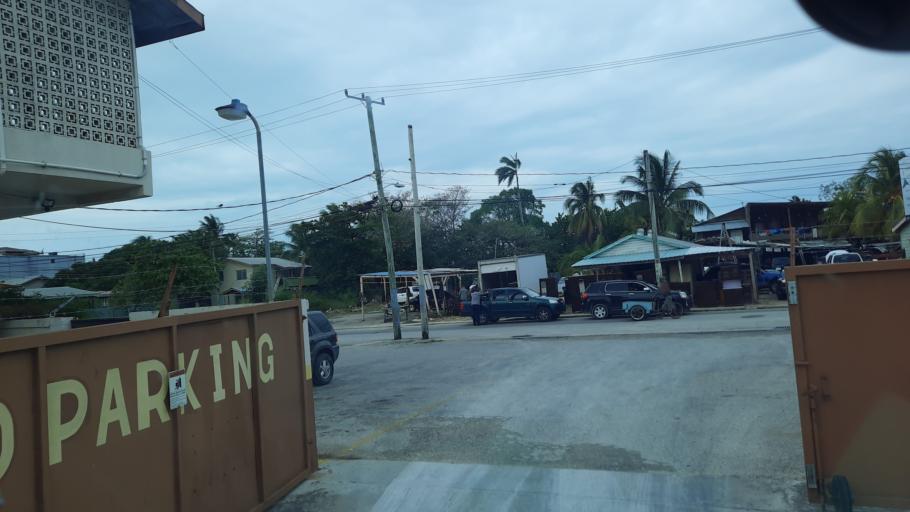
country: BZ
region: Belize
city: Belize City
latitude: 17.5001
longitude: -88.1925
